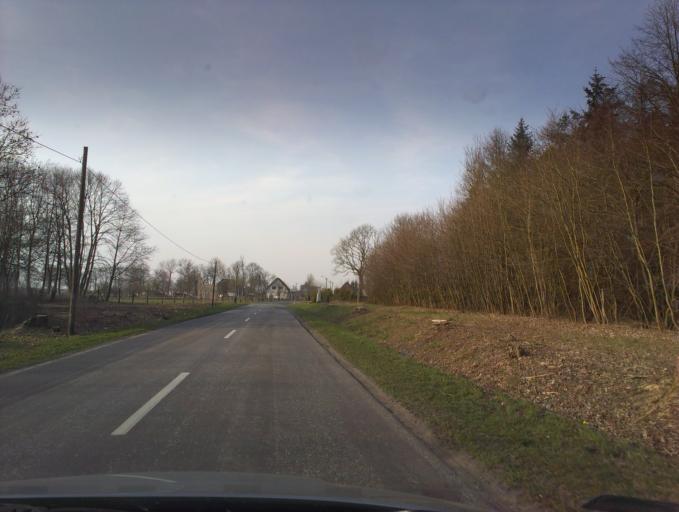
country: PL
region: Pomeranian Voivodeship
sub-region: Powiat czluchowski
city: Debrzno
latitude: 53.5218
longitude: 17.2324
